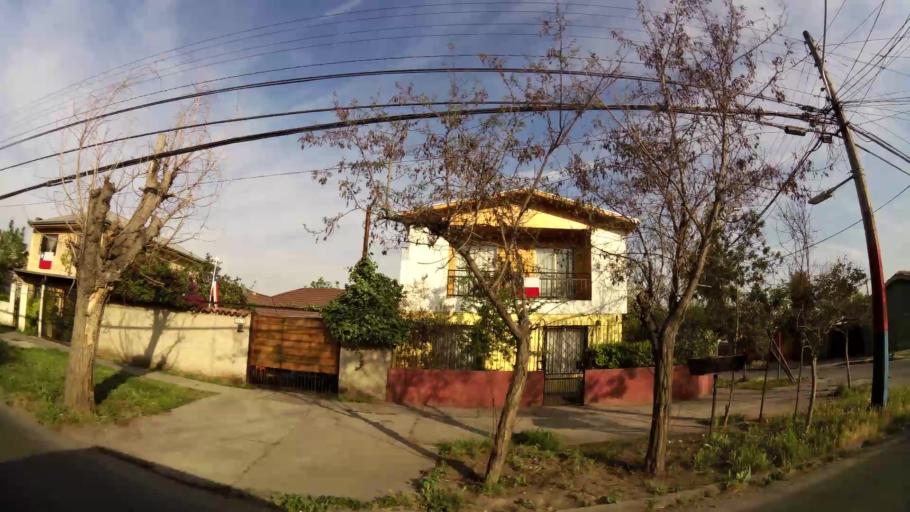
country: CL
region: Santiago Metropolitan
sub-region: Provincia de Santiago
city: La Pintana
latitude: -33.5301
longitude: -70.6711
